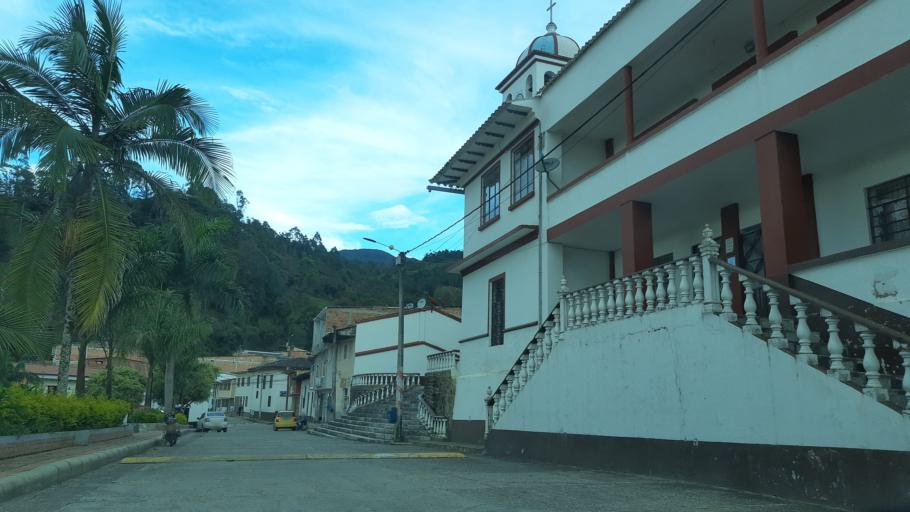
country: CO
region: Boyaca
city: Chivor
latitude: 4.9716
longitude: -73.3203
